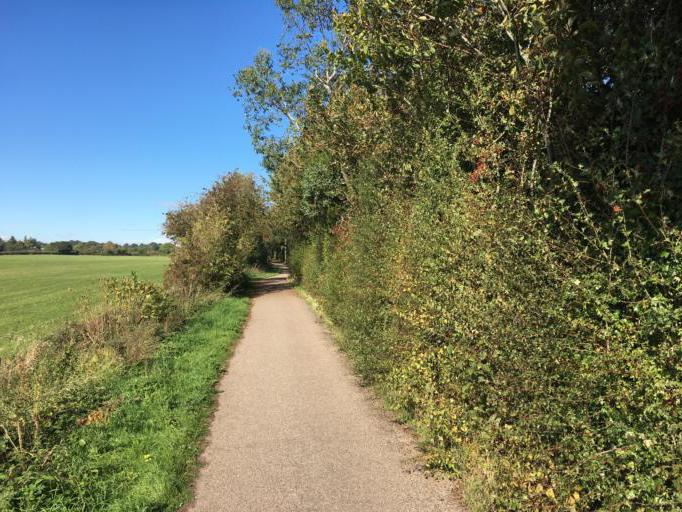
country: GB
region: England
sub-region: Warwickshire
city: Kenilworth
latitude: 52.3684
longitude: -1.5853
